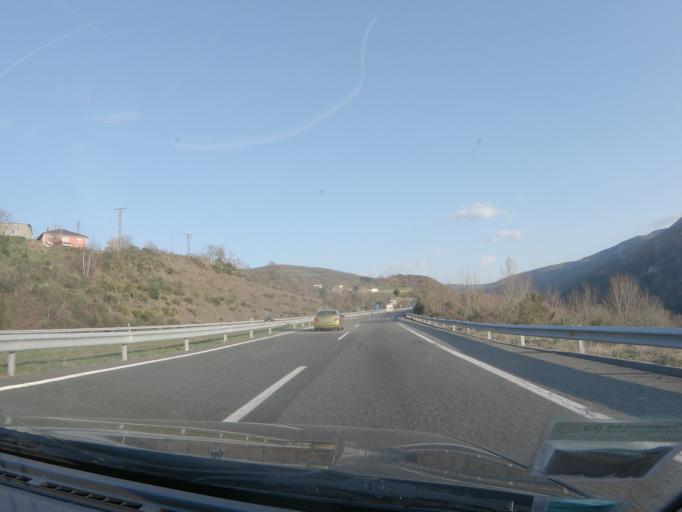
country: ES
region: Galicia
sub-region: Provincia de Lugo
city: Becerrea
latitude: 42.7803
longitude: -7.1032
